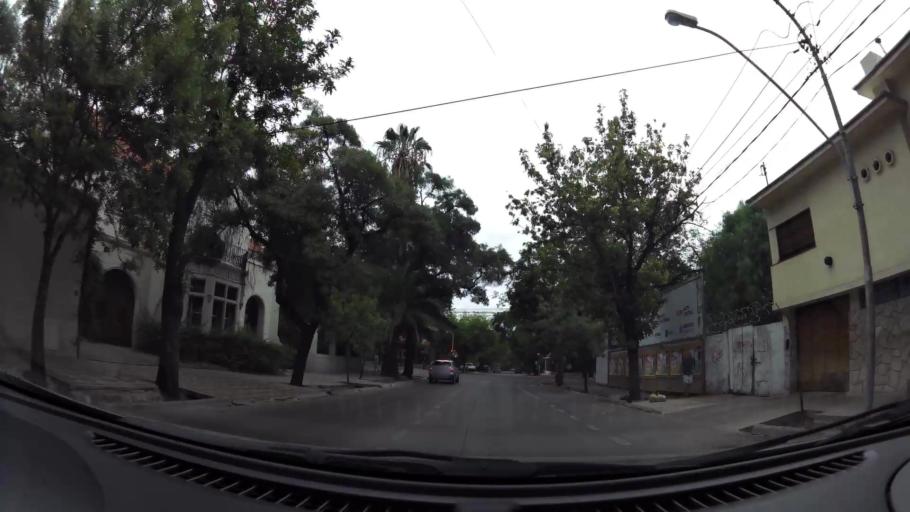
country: AR
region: Mendoza
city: Mendoza
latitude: -32.8874
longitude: -68.8590
